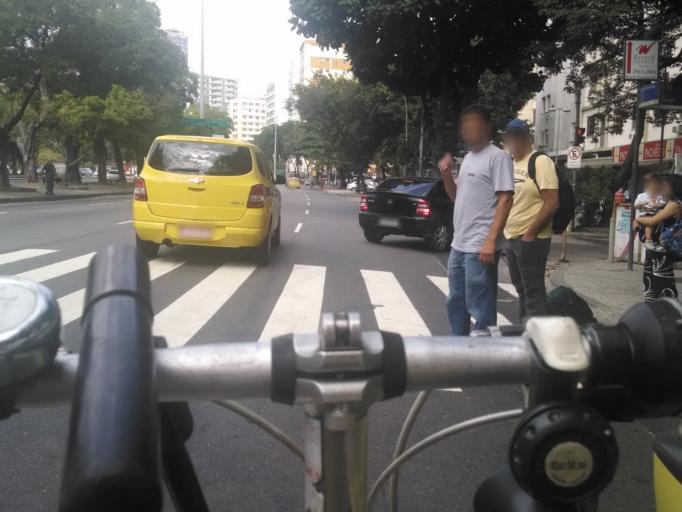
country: BR
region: Rio de Janeiro
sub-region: Rio De Janeiro
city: Rio de Janeiro
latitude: -22.9475
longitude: -43.1826
